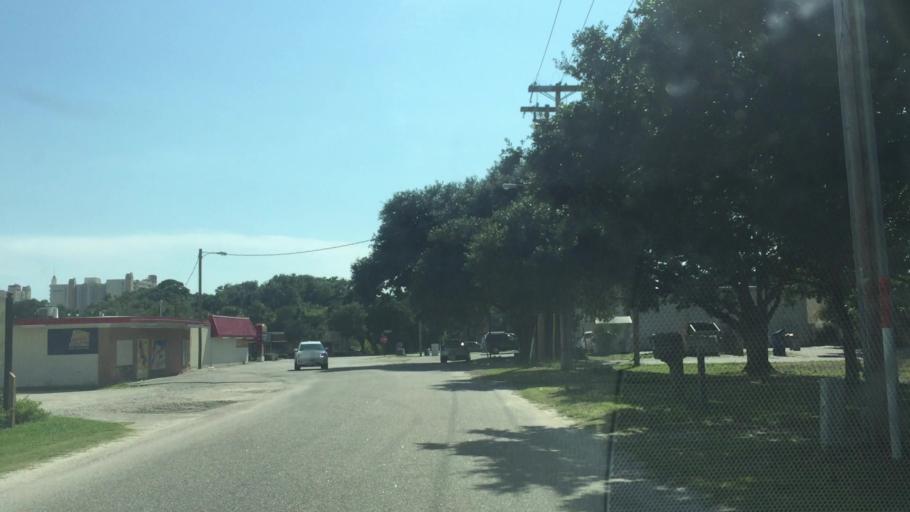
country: US
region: South Carolina
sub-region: Horry County
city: North Myrtle Beach
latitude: 33.8222
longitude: -78.6728
